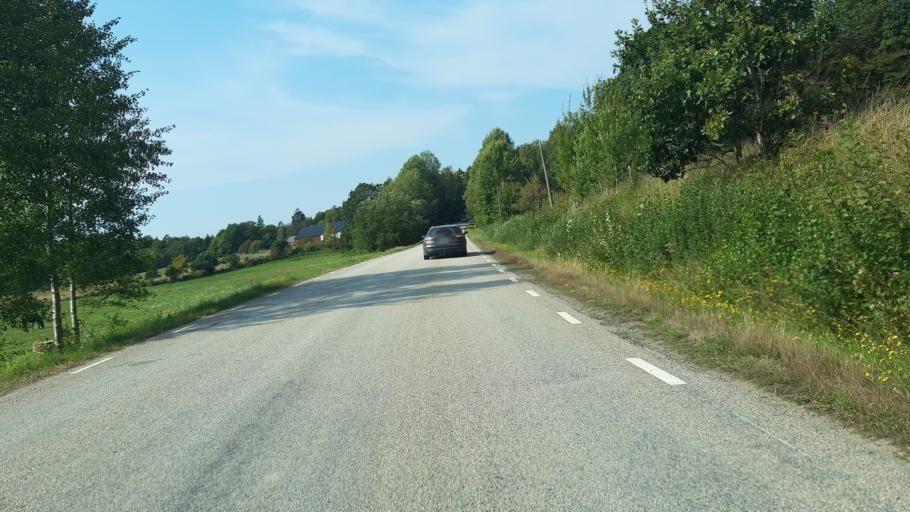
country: SE
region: Blekinge
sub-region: Ronneby Kommun
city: Brakne-Hoby
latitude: 56.1725
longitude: 15.1390
